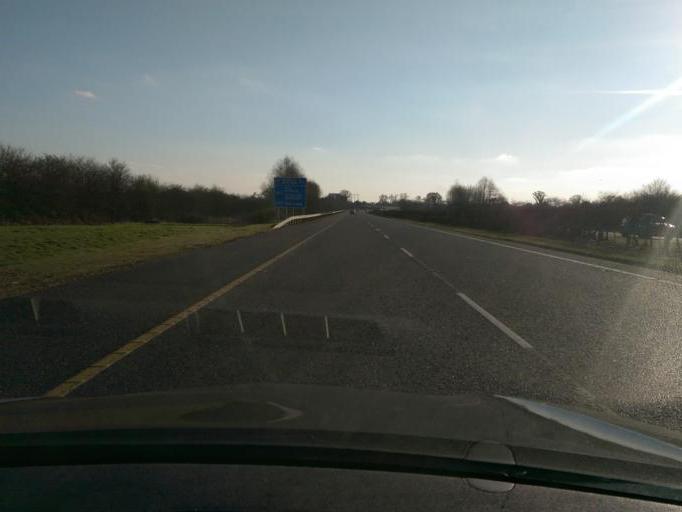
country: IE
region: Leinster
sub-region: Laois
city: Portlaoise
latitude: 53.0235
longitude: -7.2590
